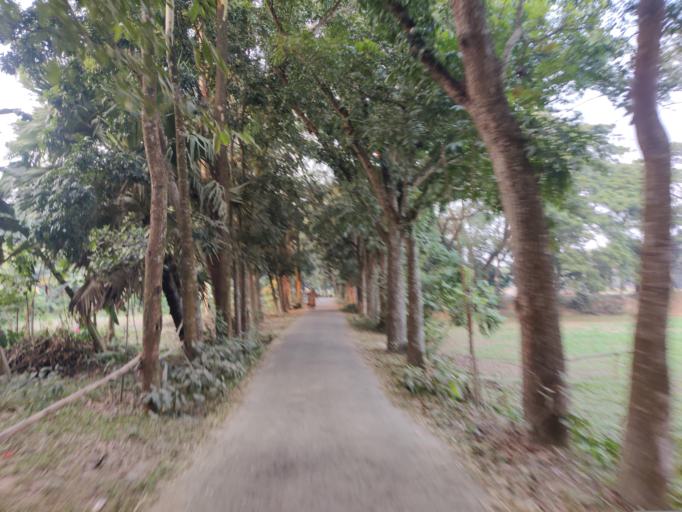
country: BD
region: Dhaka
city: Bajitpur
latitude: 24.1573
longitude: 90.7615
